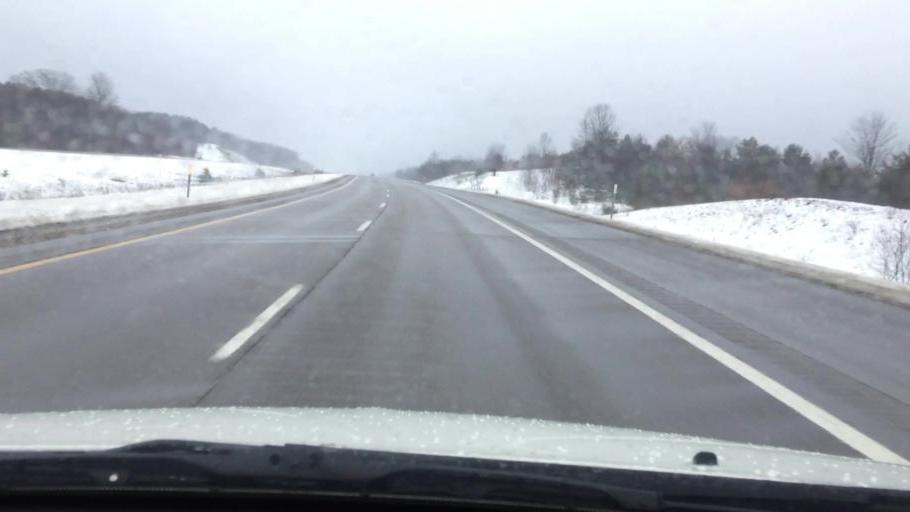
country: US
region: Michigan
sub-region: Wexford County
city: Manton
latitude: 44.3666
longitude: -85.4023
